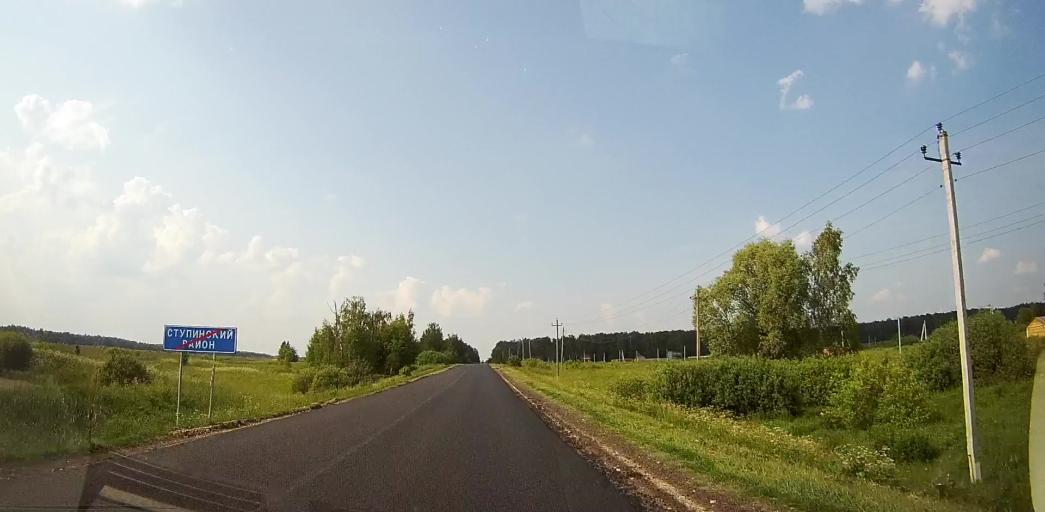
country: RU
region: Moskovskaya
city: Il'inskoye
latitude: 55.2284
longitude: 37.9240
